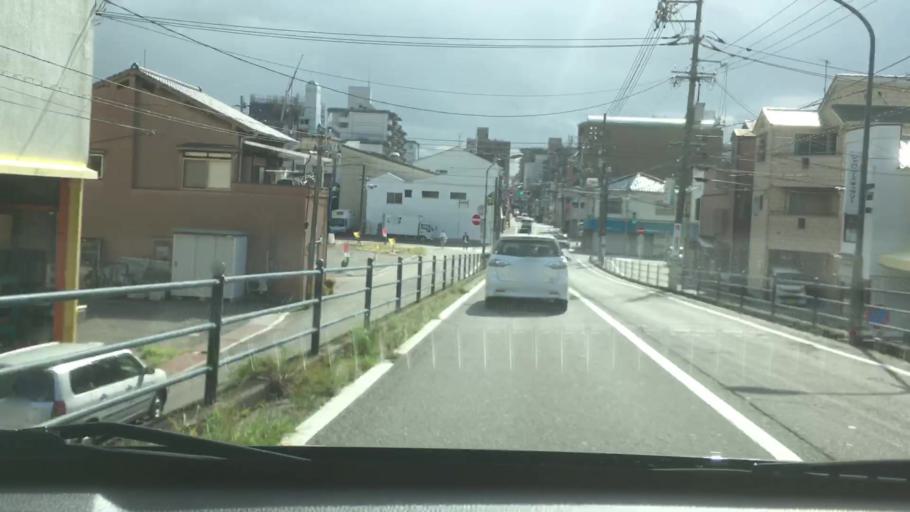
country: JP
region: Hiroshima
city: Hiroshima-shi
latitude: 34.3982
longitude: 132.4346
